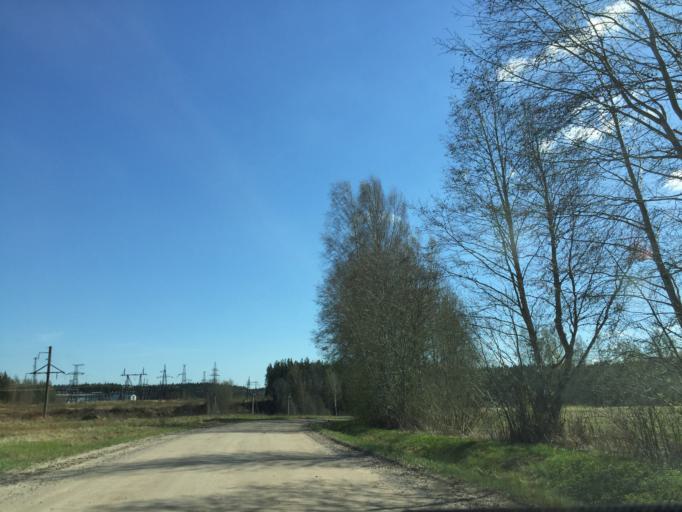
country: EE
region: Valgamaa
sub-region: Valga linn
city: Valga
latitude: 57.8532
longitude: 26.1700
